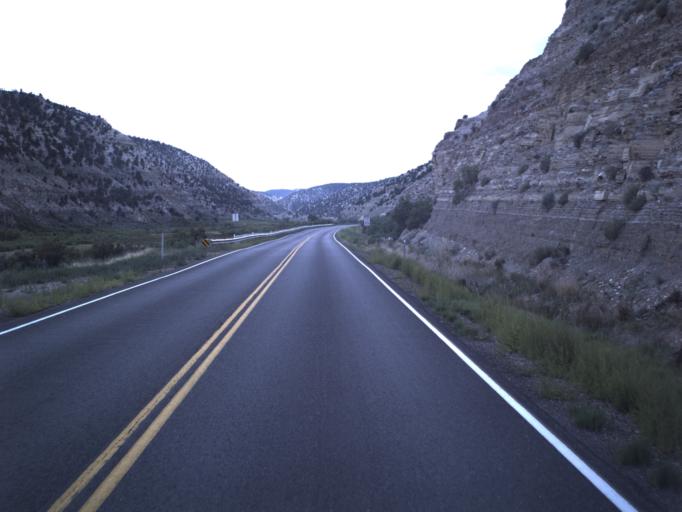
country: US
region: Utah
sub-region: Duchesne County
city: Duchesne
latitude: 40.1026
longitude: -110.4753
